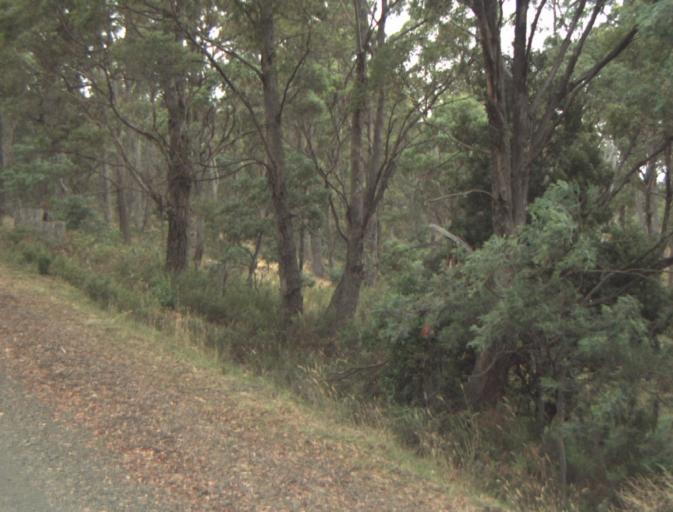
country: AU
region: Tasmania
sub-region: Northern Midlands
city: Evandale
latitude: -41.4820
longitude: 147.5361
